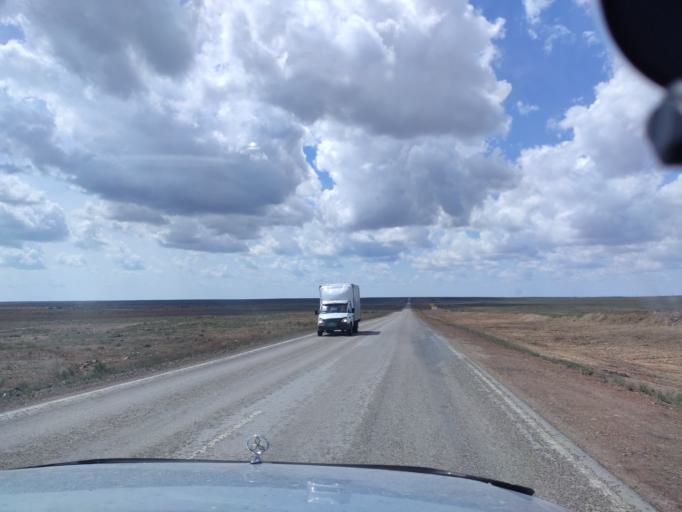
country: KZ
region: Qaraghandy
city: Saryshaghan
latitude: 46.0043
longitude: 73.5831
